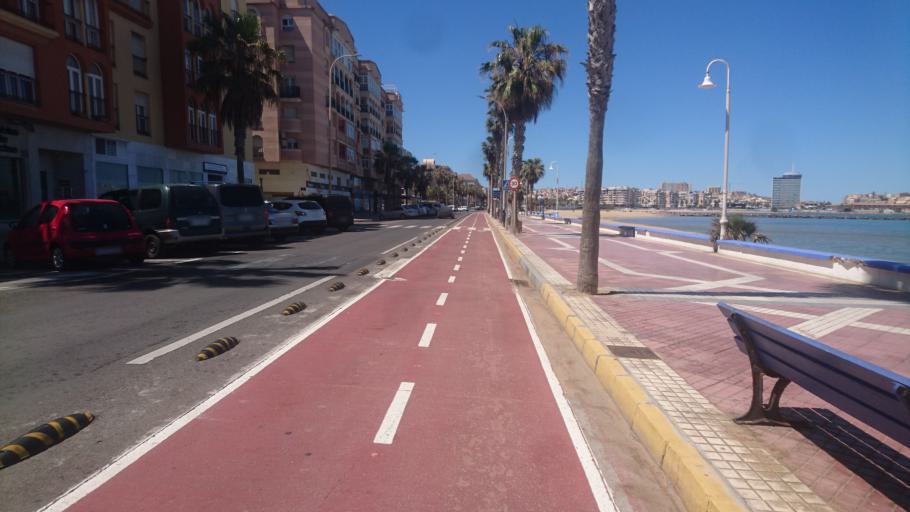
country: ES
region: Melilla
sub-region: Melilla
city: Melilla
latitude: 35.2802
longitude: -2.9368
